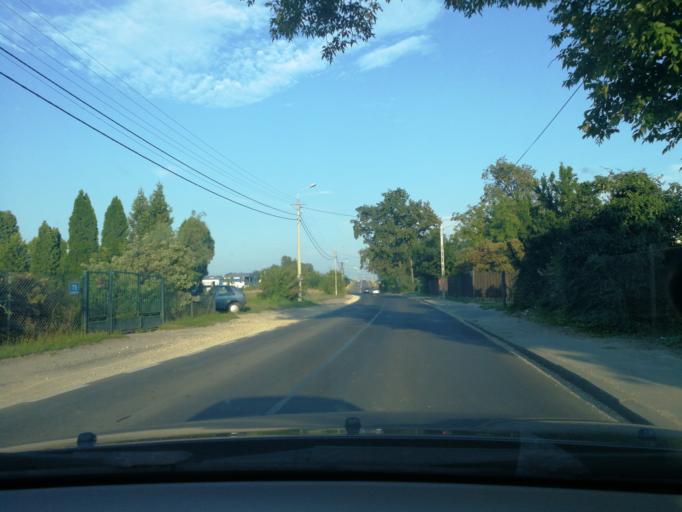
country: PL
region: Masovian Voivodeship
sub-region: Powiat warszawski zachodni
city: Ozarow Mazowiecki
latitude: 52.1863
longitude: 20.7677
